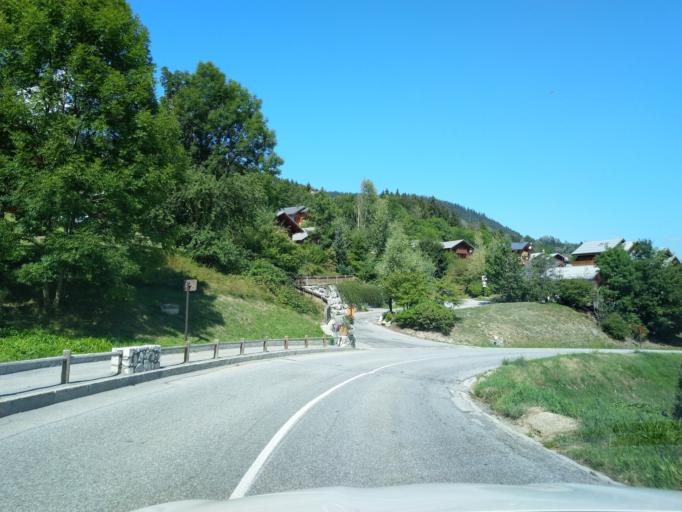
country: FR
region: Rhone-Alpes
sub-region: Departement de la Savoie
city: Les Allues
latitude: 45.4338
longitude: 6.5559
